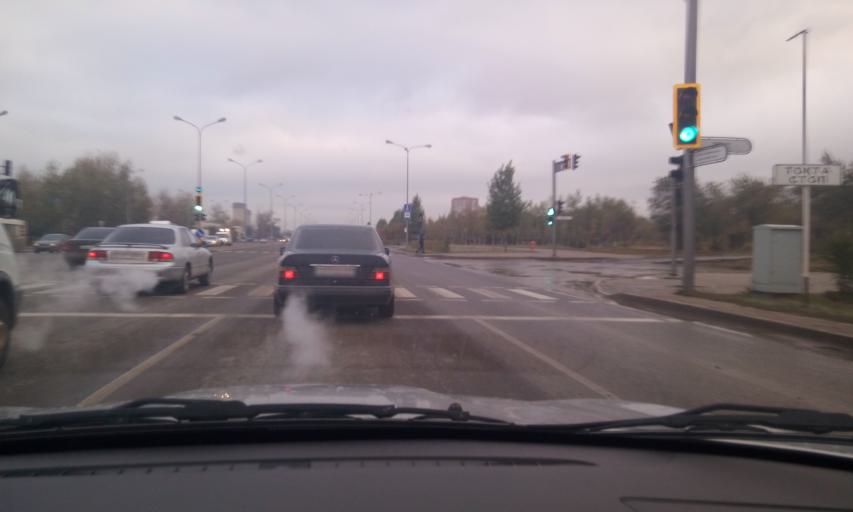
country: KZ
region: Astana Qalasy
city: Astana
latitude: 51.1840
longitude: 71.3633
